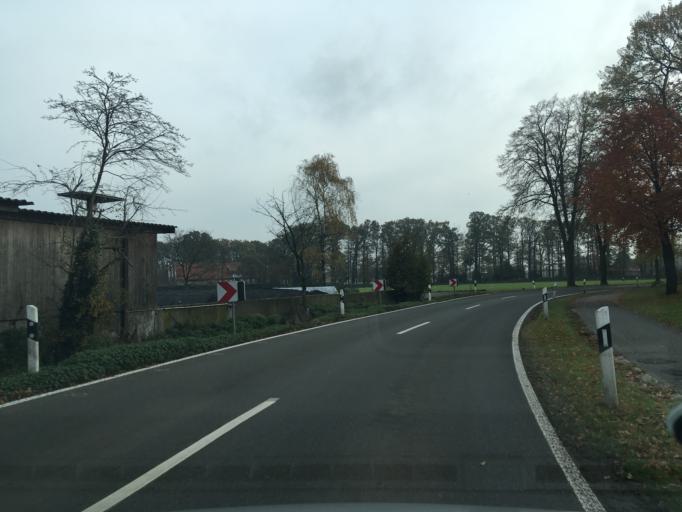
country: DE
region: North Rhine-Westphalia
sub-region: Regierungsbezirk Munster
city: Velen
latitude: 51.9288
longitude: 6.9507
